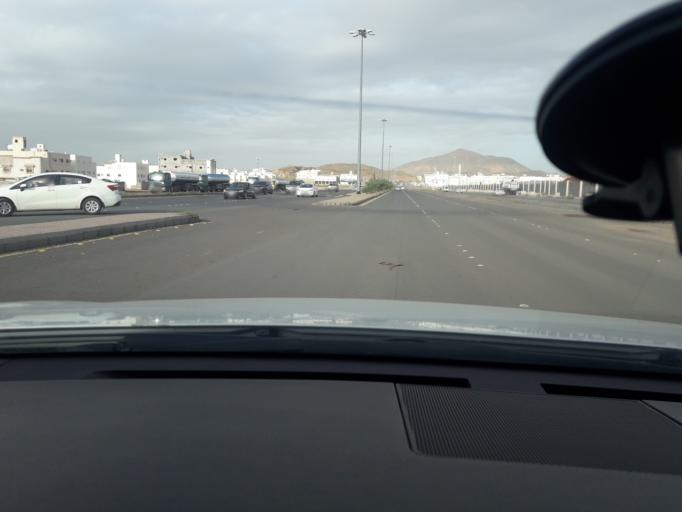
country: SA
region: Al Madinah al Munawwarah
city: Sultanah
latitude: 24.4646
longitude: 39.5149
